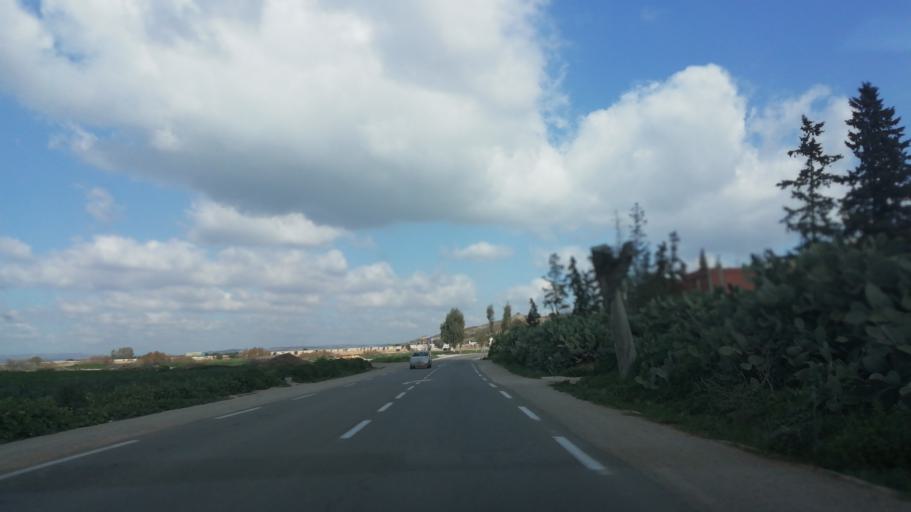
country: DZ
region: Mostaganem
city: Mostaganem
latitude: 35.7014
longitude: 0.2227
